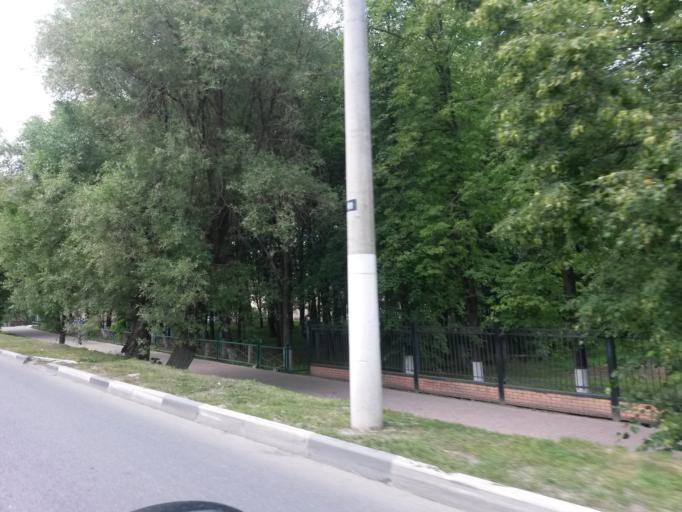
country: RU
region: Moskovskaya
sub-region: Chekhovskiy Rayon
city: Chekhov
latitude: 55.1465
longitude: 37.4798
